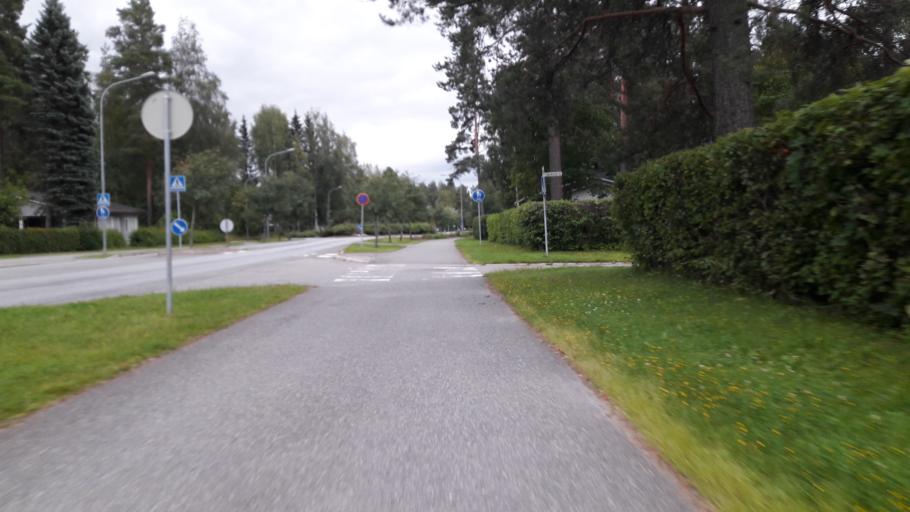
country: FI
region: North Karelia
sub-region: Joensuu
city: Joensuu
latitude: 62.6109
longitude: 29.7360
